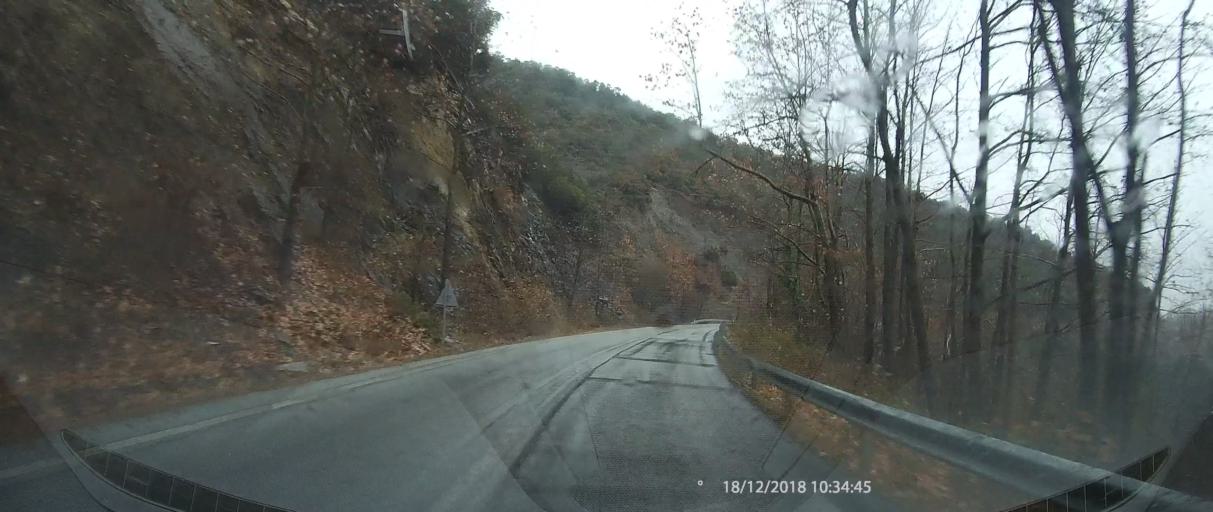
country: GR
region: Central Macedonia
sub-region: Nomos Pierias
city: Kato Milia
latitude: 40.2103
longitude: 22.3017
